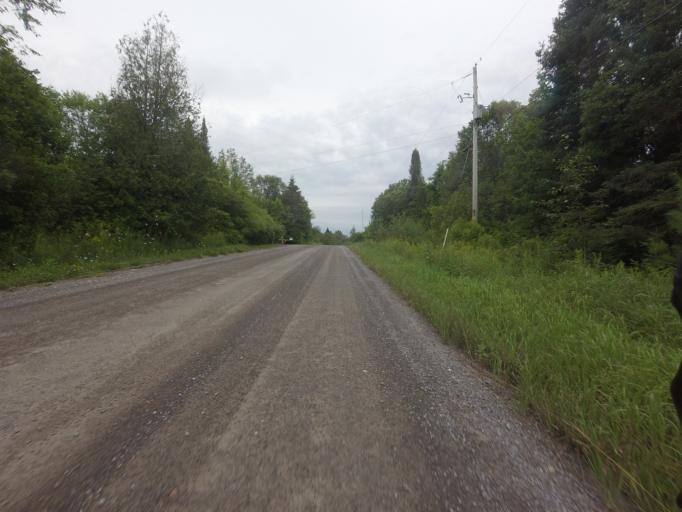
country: CA
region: Ontario
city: Carleton Place
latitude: 45.1615
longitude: -76.2702
